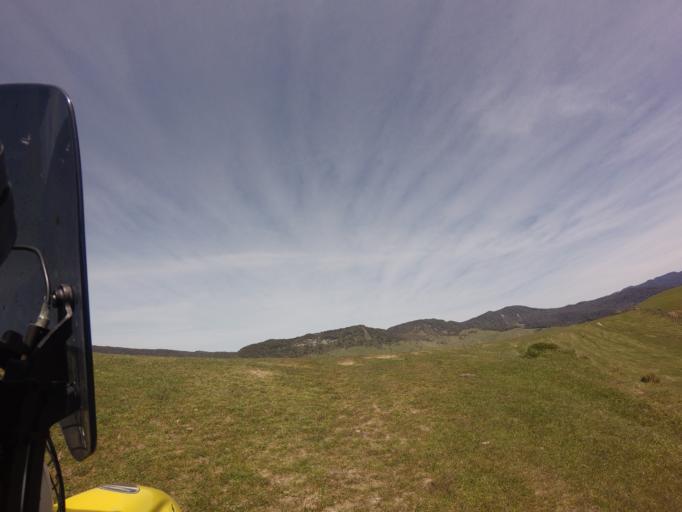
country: NZ
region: Bay of Plenty
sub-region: Opotiki District
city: Opotiki
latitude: -38.4717
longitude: 177.3787
